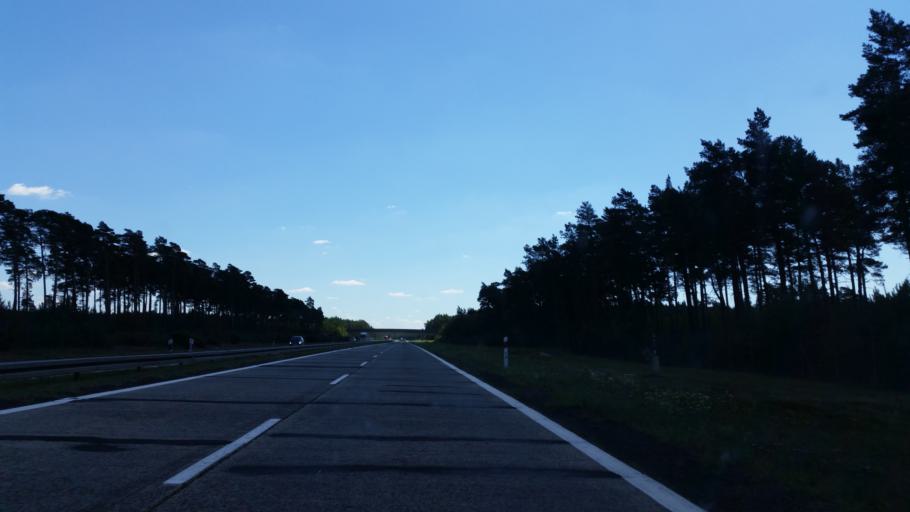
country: PL
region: Lower Silesian Voivodeship
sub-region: Powiat boleslawiecki
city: Boleslawiec
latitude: 51.3783
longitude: 15.5535
